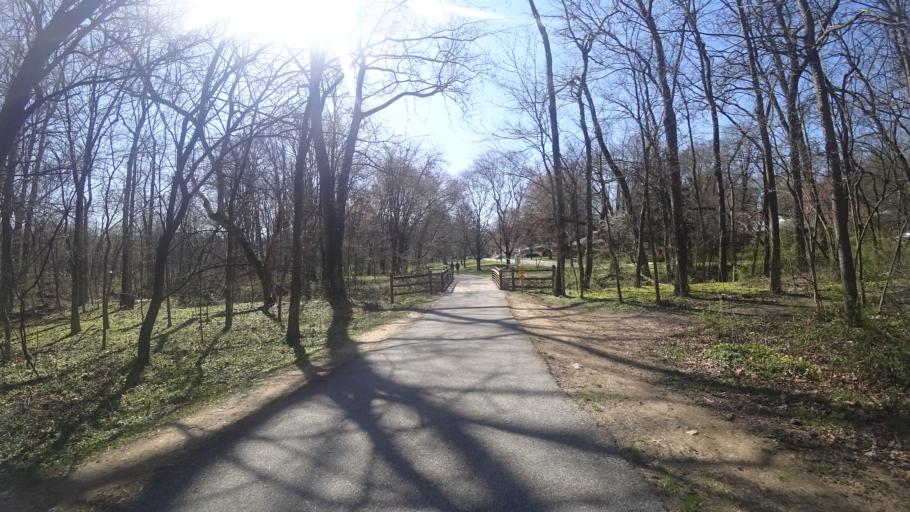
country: US
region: Maryland
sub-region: Montgomery County
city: Four Corners
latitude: 39.0132
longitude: -77.0320
